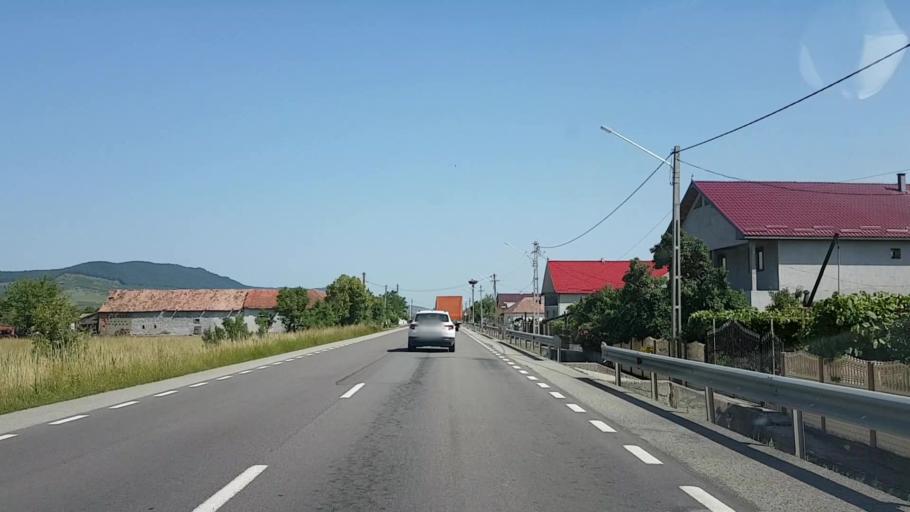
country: RO
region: Bistrita-Nasaud
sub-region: Comuna Sieu-Odorhei
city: Sieu-Odorhei
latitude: 47.1183
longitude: 24.3318
